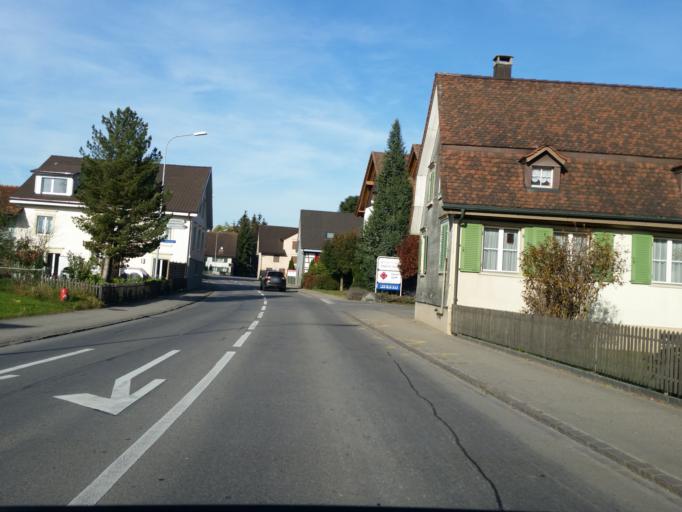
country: CH
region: Thurgau
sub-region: Arbon District
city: Amriswil
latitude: 47.5507
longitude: 9.2730
